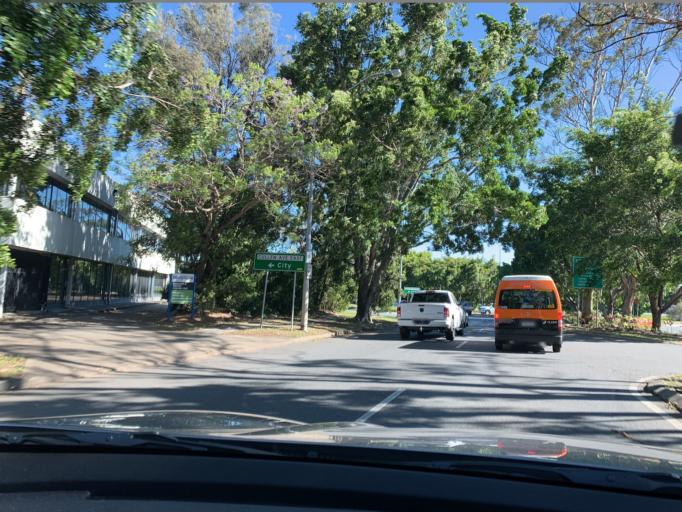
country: AU
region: Queensland
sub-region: Brisbane
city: Ascot
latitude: -27.4336
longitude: 153.0880
